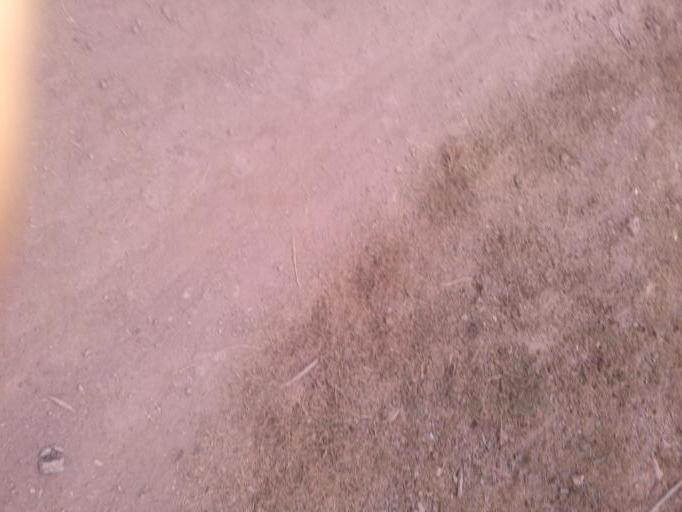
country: LA
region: Xiangkhoang
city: Muang Phonsavan
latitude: 19.3354
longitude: 103.6567
